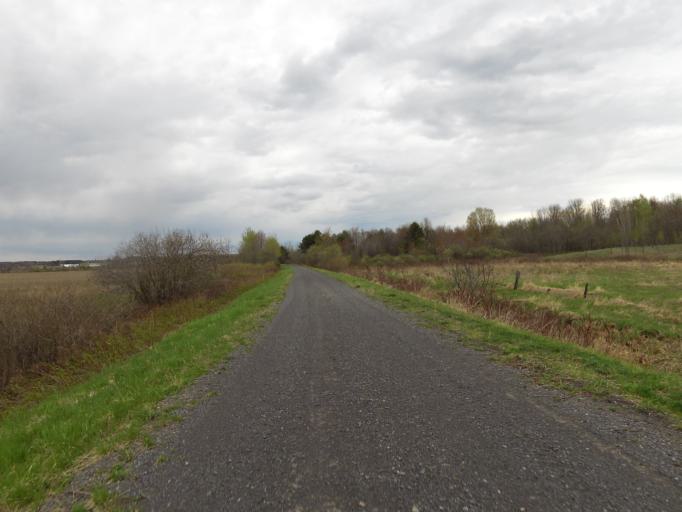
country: CA
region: Quebec
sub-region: Outaouais
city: Papineauville
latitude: 45.5196
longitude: -74.9695
